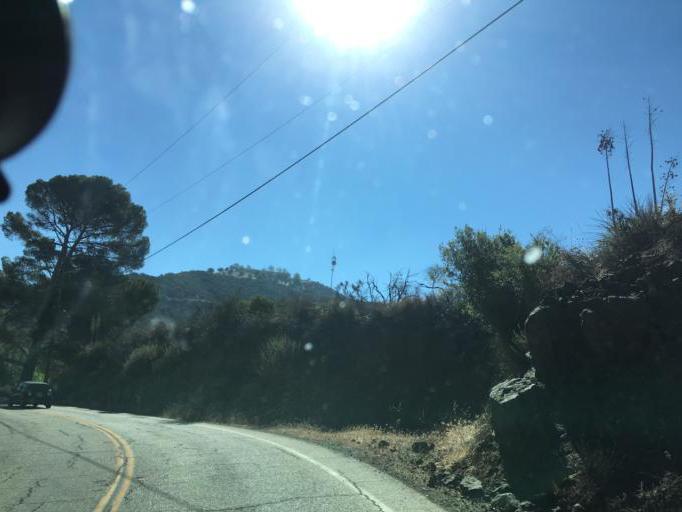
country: US
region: California
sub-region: Ventura County
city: Thousand Oaks
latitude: 34.0890
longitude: -118.8915
